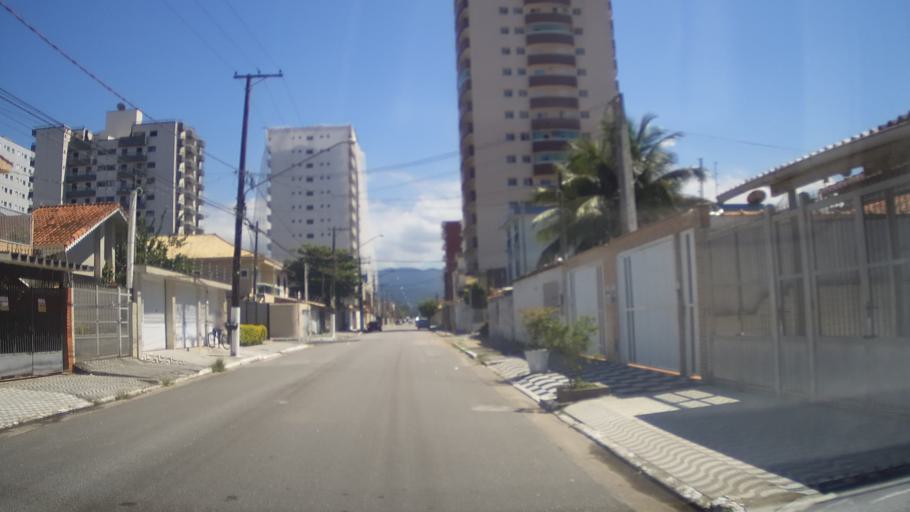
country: BR
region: Sao Paulo
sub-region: Praia Grande
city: Praia Grande
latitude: -24.0272
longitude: -46.4745
